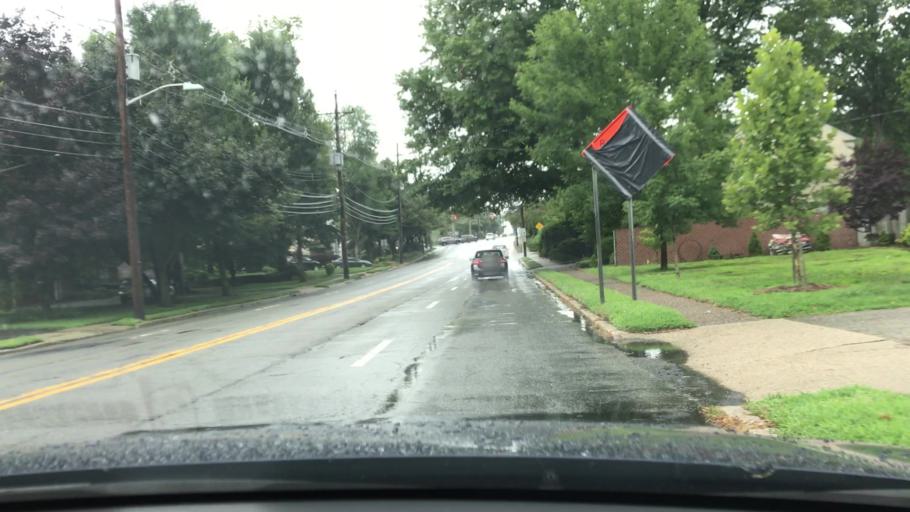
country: US
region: New Jersey
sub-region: Bergen County
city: Oradell
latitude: 40.9612
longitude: -74.0578
